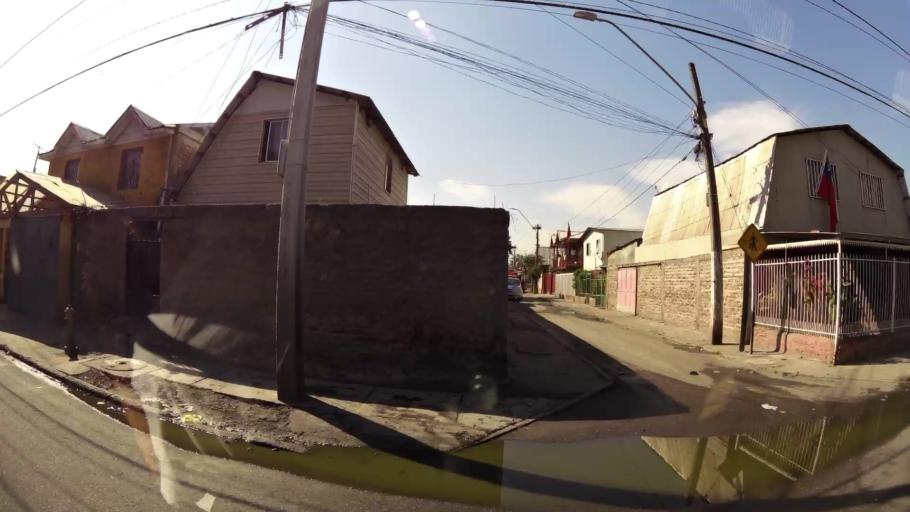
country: CL
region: Santiago Metropolitan
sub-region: Provincia de Maipo
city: San Bernardo
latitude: -33.5963
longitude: -70.6866
